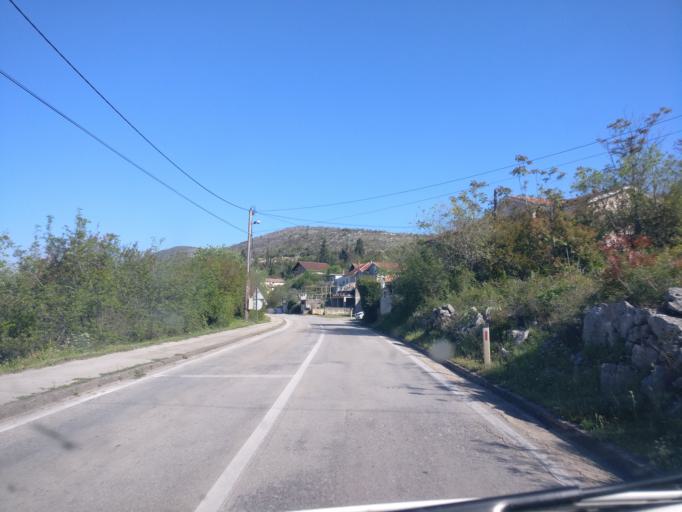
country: BA
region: Federation of Bosnia and Herzegovina
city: Capljina
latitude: 43.1334
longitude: 17.6754
